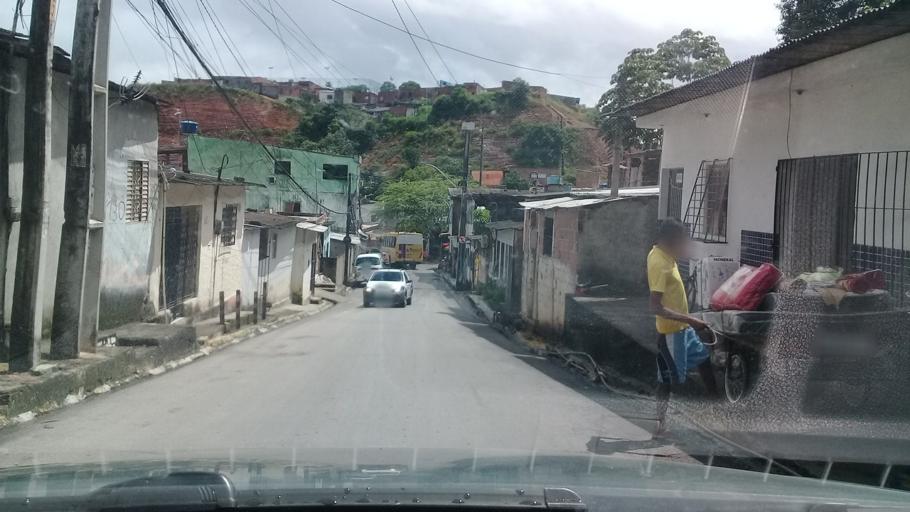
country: BR
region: Pernambuco
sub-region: Jaboatao Dos Guararapes
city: Jaboatao dos Guararapes
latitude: -8.1102
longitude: -34.9543
